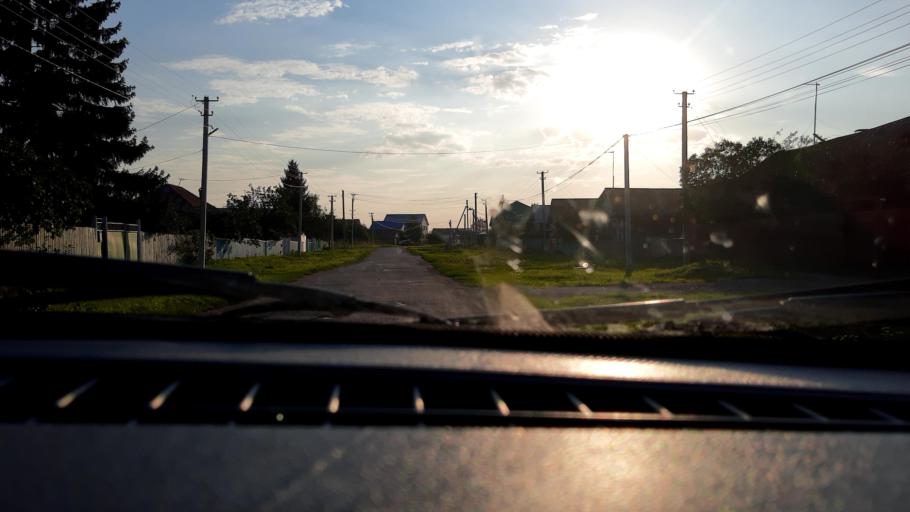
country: RU
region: Bashkortostan
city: Mikhaylovka
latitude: 54.8908
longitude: 55.9107
